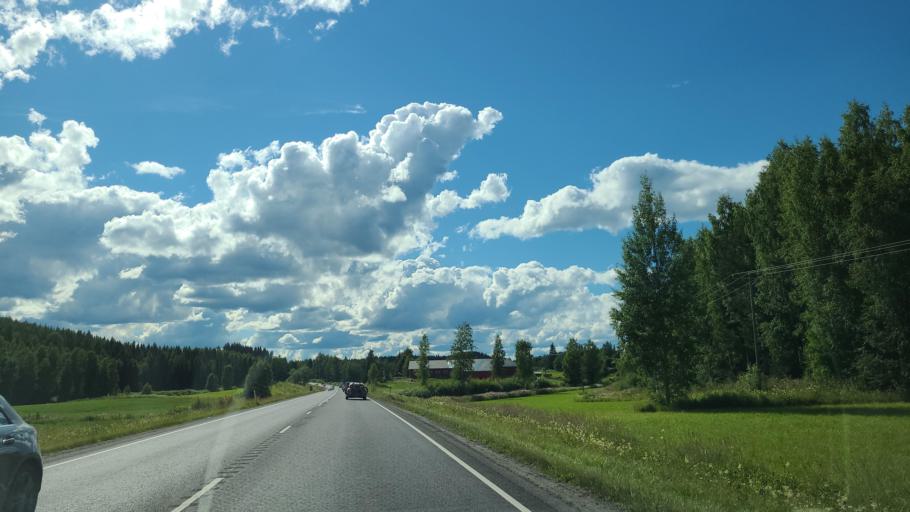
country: FI
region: Central Finland
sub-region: Jyvaeskylae
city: Korpilahti
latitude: 61.9921
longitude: 25.4440
